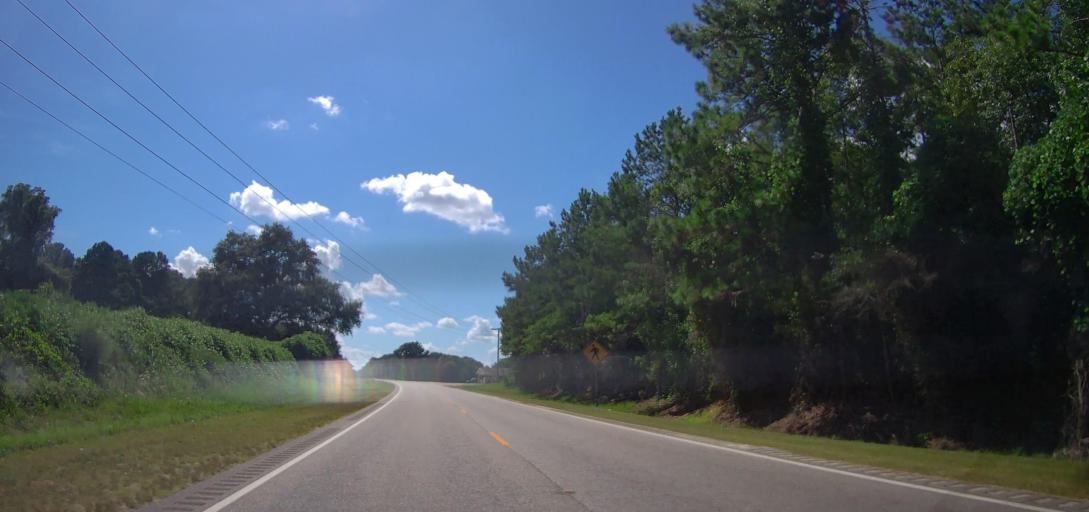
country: US
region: Alabama
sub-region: Elmore County
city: Tallassee
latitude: 32.3977
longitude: -85.9143
